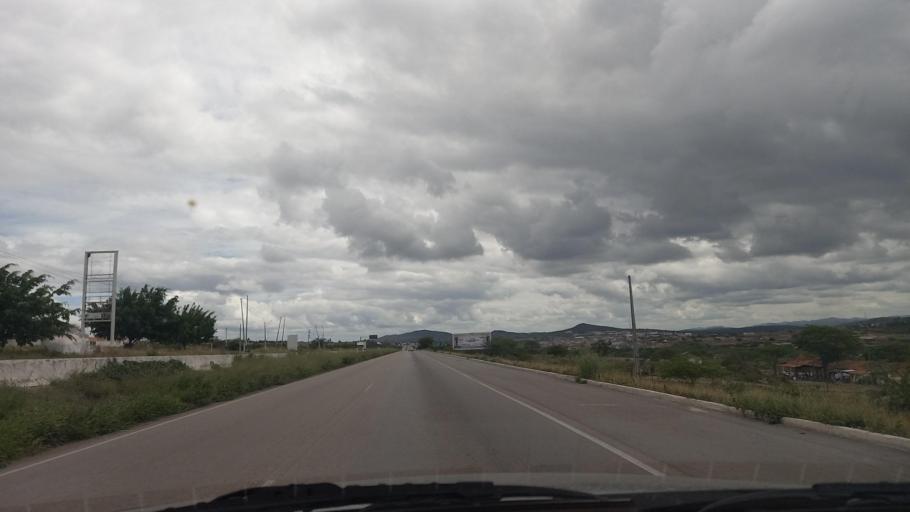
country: BR
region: Pernambuco
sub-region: Caruaru
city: Caruaru
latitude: -8.3250
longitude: -36.1118
